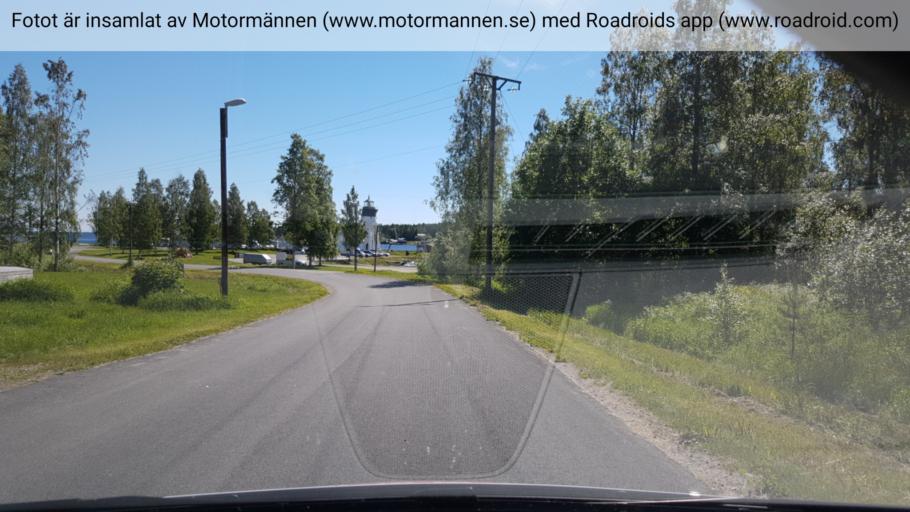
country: SE
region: Norrbotten
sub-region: Pitea Kommun
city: Pitea
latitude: 65.1463
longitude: 21.5054
